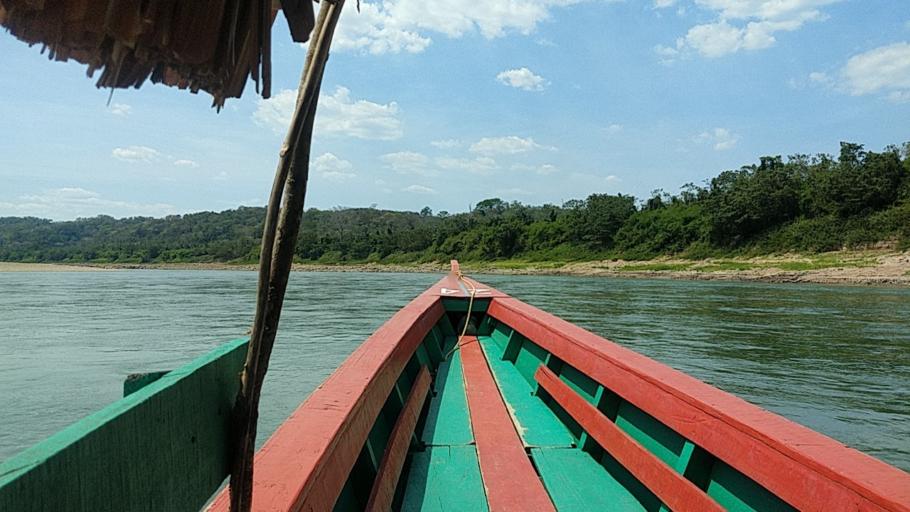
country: MX
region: Chiapas
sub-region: Ocosingo
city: Frontera Corozal
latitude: 16.8953
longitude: -90.9566
